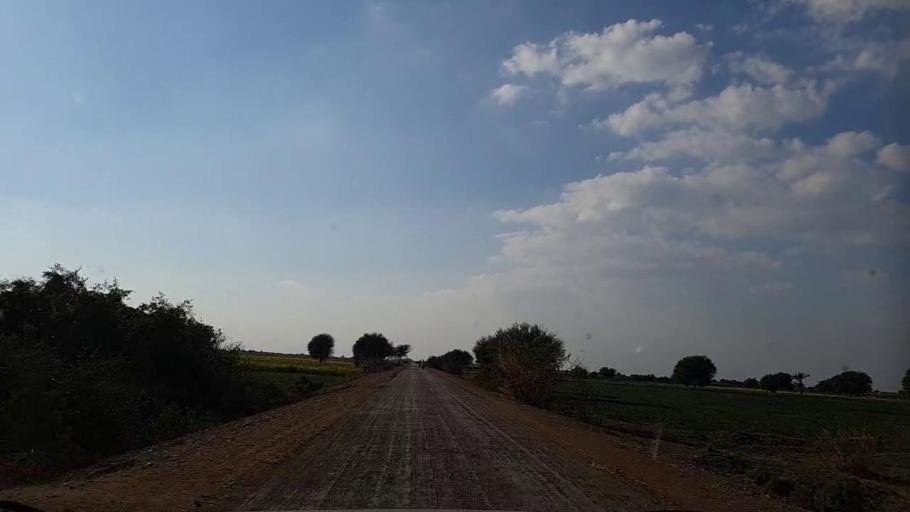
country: PK
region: Sindh
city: Pithoro
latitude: 25.6517
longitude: 69.2572
